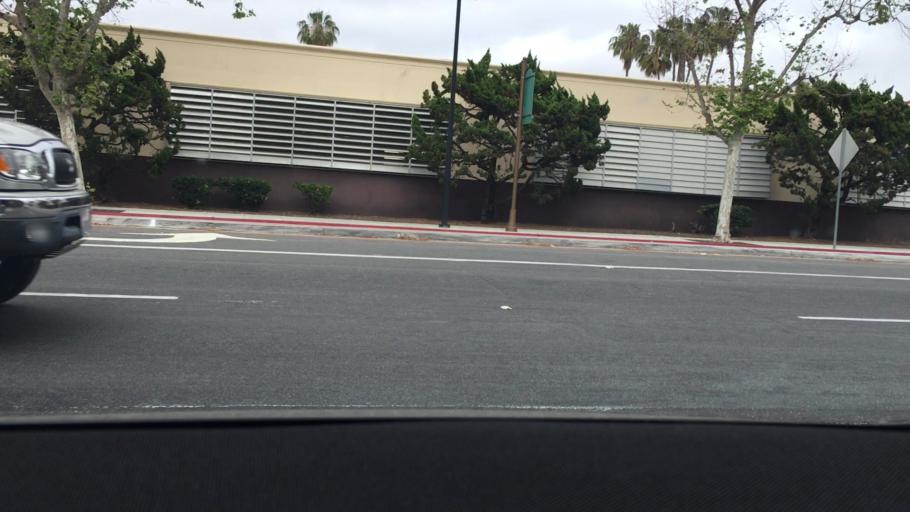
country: US
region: California
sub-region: San Diego County
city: Chula Vista
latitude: 32.6350
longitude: -117.0776
